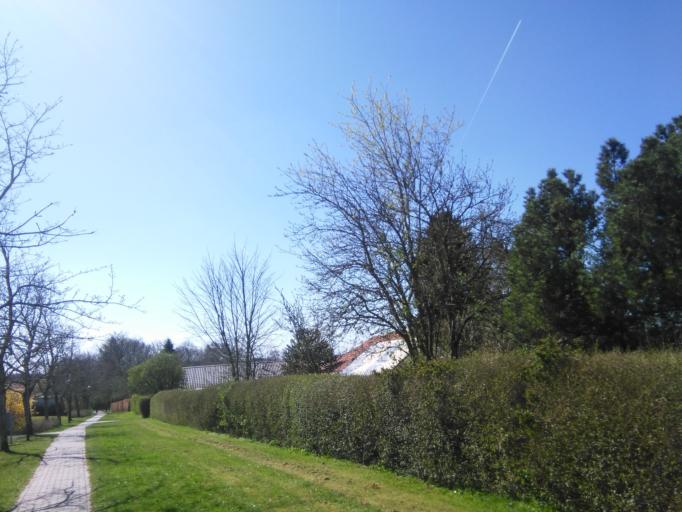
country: DK
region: Central Jutland
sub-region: Arhus Kommune
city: Marslet
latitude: 56.0734
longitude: 10.1527
